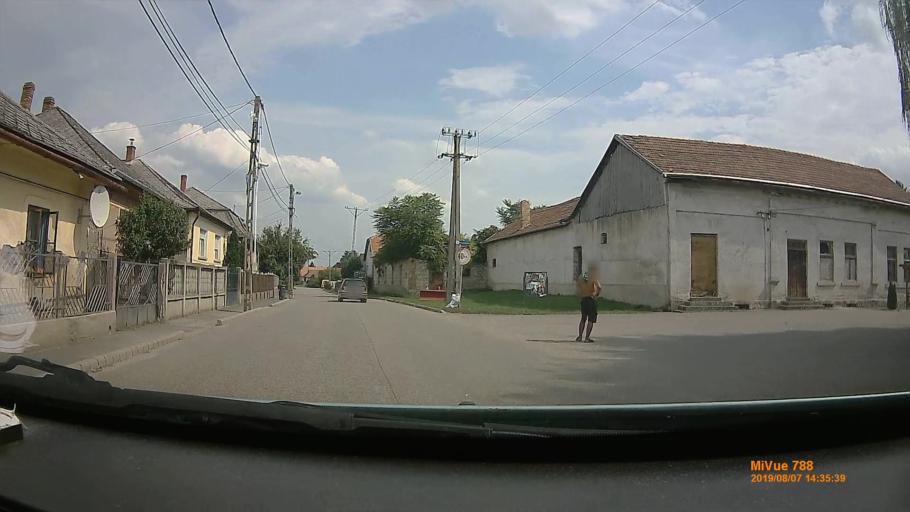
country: HU
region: Borsod-Abauj-Zemplen
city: Szikszo
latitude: 48.2051
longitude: 20.9292
